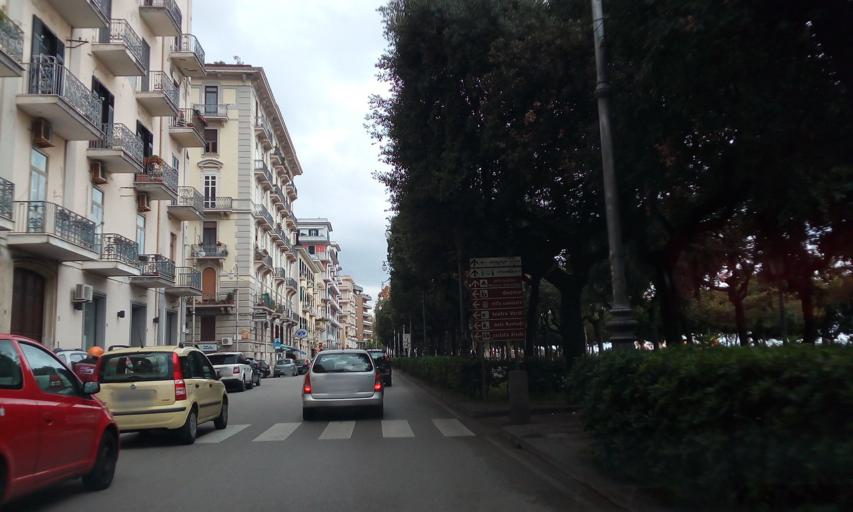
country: IT
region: Campania
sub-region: Provincia di Salerno
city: Capezzano Inferiore
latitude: 40.6755
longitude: 14.7661
